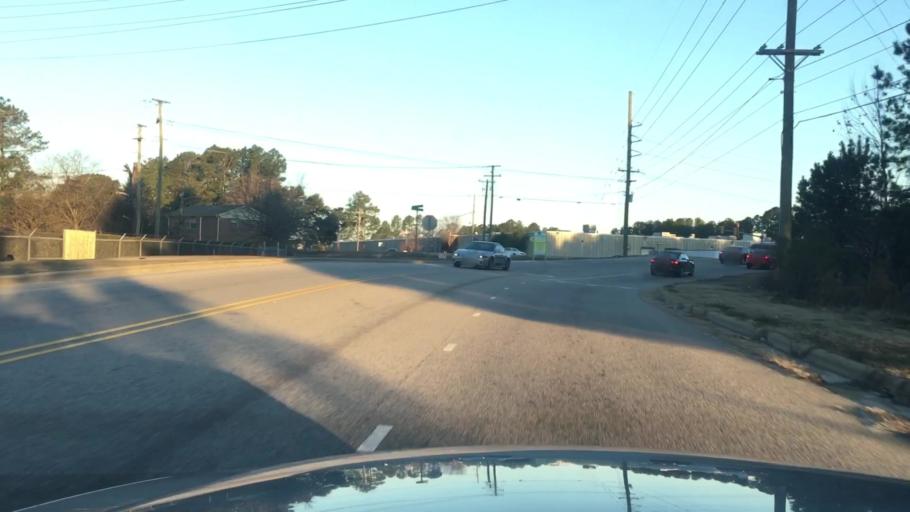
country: US
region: North Carolina
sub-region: Cumberland County
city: Hope Mills
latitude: 34.9995
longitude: -78.9045
